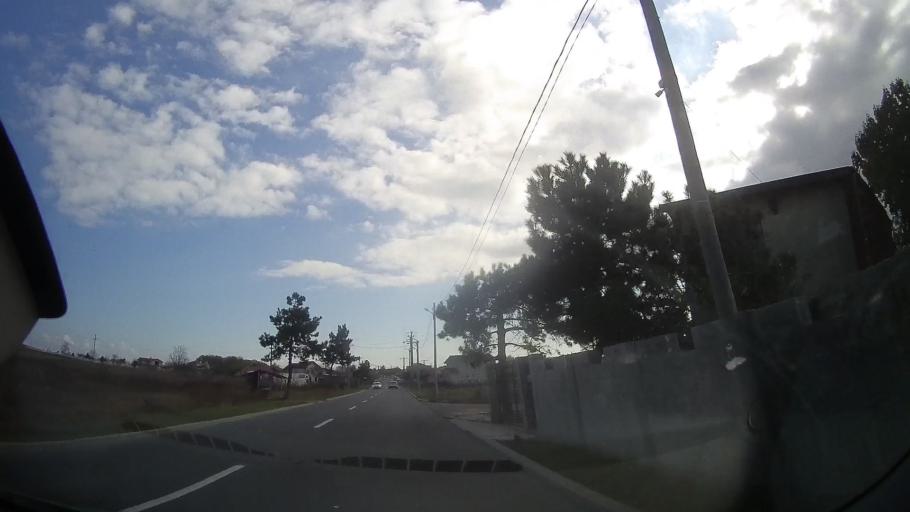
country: RO
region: Constanta
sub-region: Oras Techirghiol
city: Techirghiol
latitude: 44.0640
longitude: 28.5954
